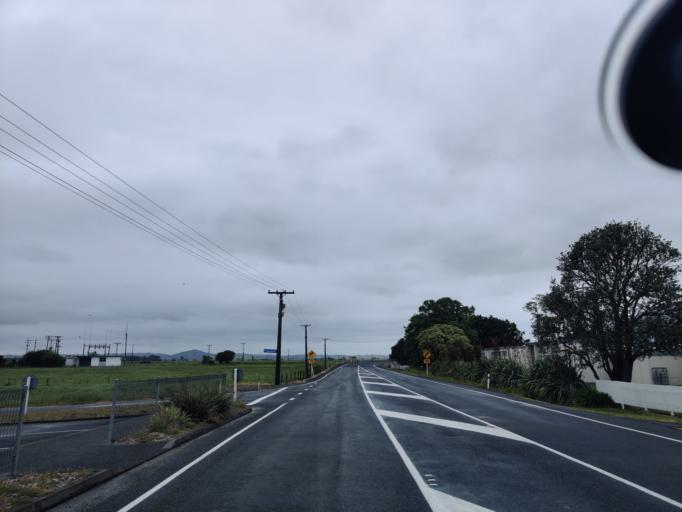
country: NZ
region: Northland
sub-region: Kaipara District
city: Dargaville
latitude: -36.1219
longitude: 174.0113
